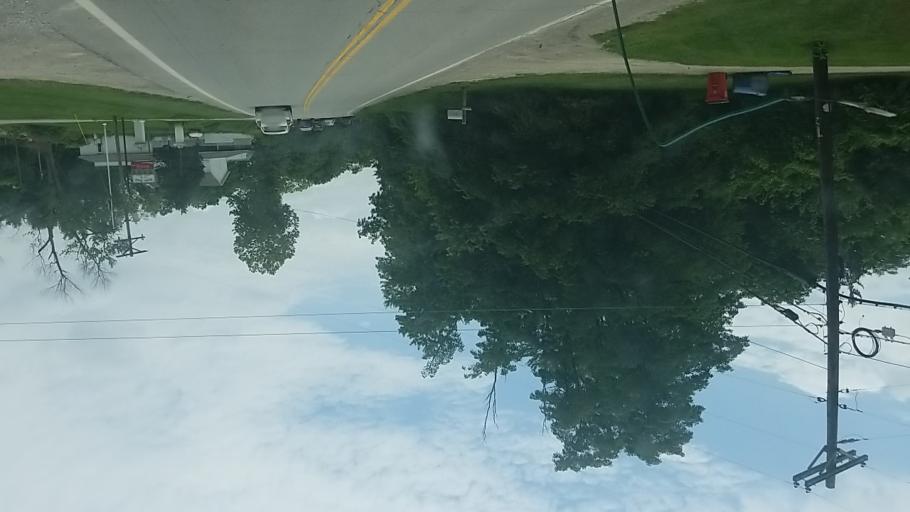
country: US
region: Ohio
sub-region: Franklin County
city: Obetz
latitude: 39.8320
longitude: -82.9839
